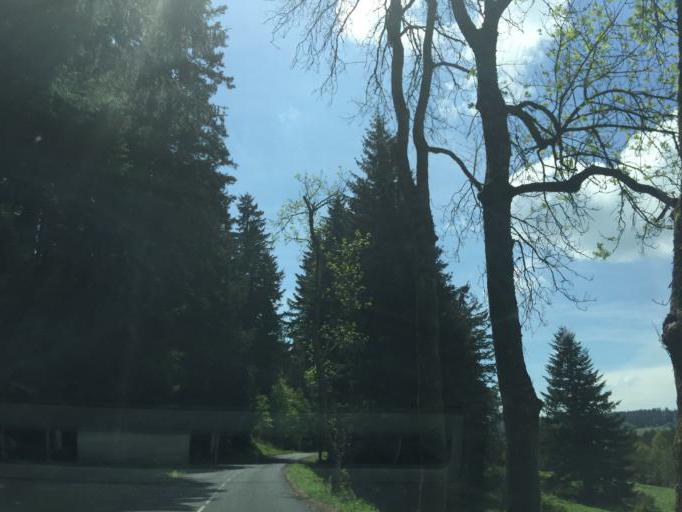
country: FR
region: Rhone-Alpes
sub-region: Departement de la Loire
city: Saint-Sauveur-en-Rue
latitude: 45.2935
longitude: 4.4517
